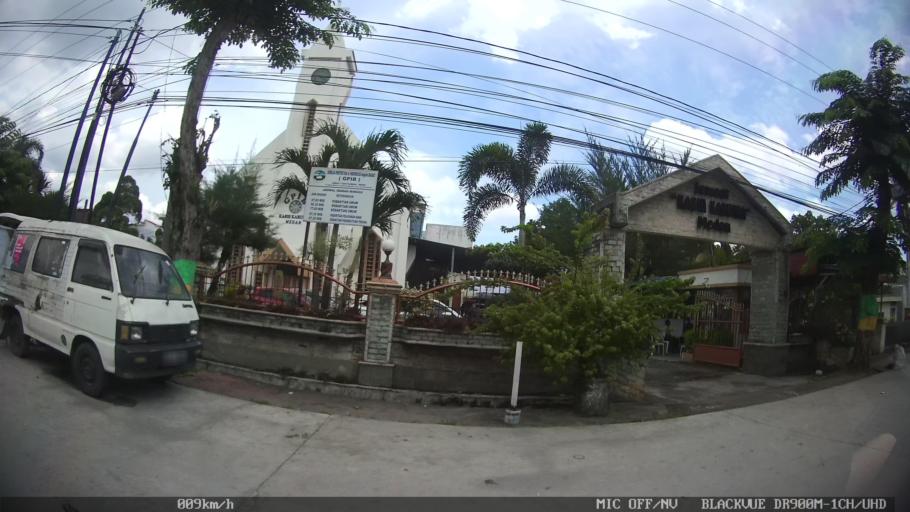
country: ID
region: North Sumatra
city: Medan
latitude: 3.5992
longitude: 98.6451
